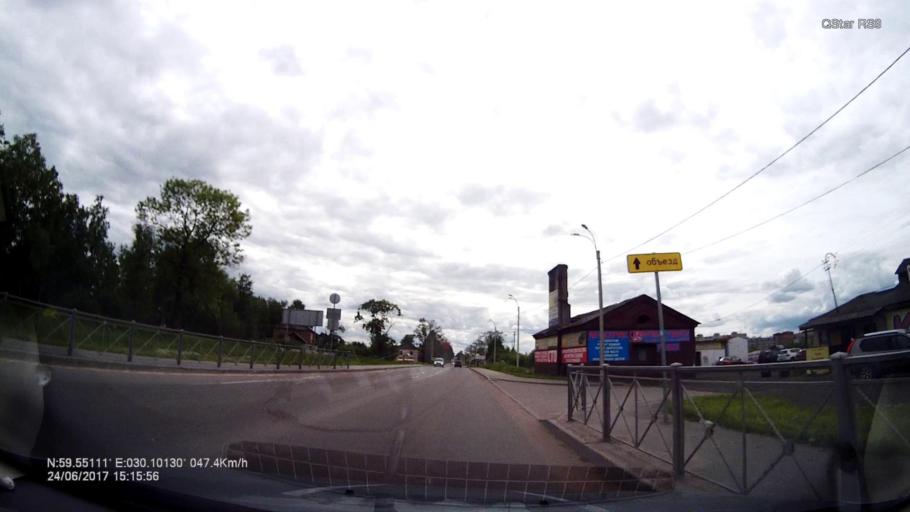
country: RU
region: Leningrad
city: Gatchina
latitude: 59.5511
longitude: 30.1012
